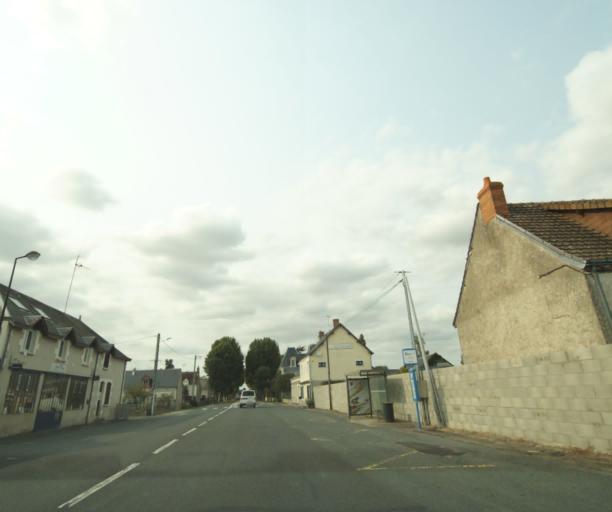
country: FR
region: Centre
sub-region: Departement de l'Indre
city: Chatillon-sur-Indre
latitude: 47.0206
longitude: 1.1073
